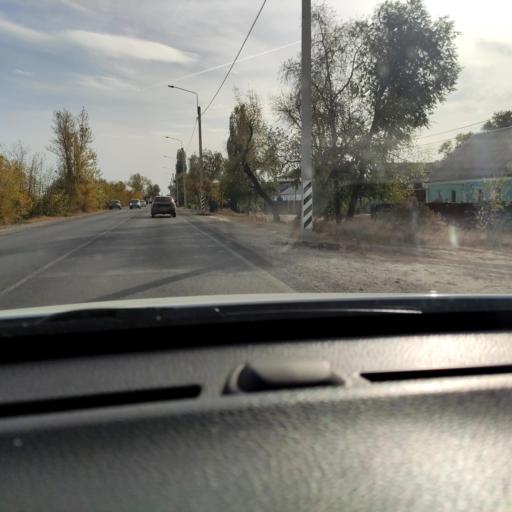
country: RU
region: Voronezj
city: Maslovka
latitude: 51.5693
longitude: 39.2461
